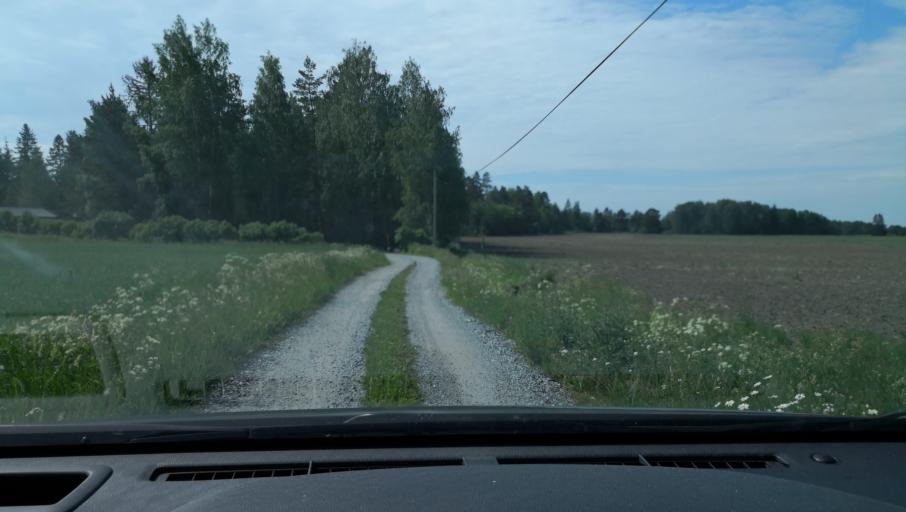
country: SE
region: Uppsala
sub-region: Enkopings Kommun
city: Enkoping
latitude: 59.7029
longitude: 17.1389
